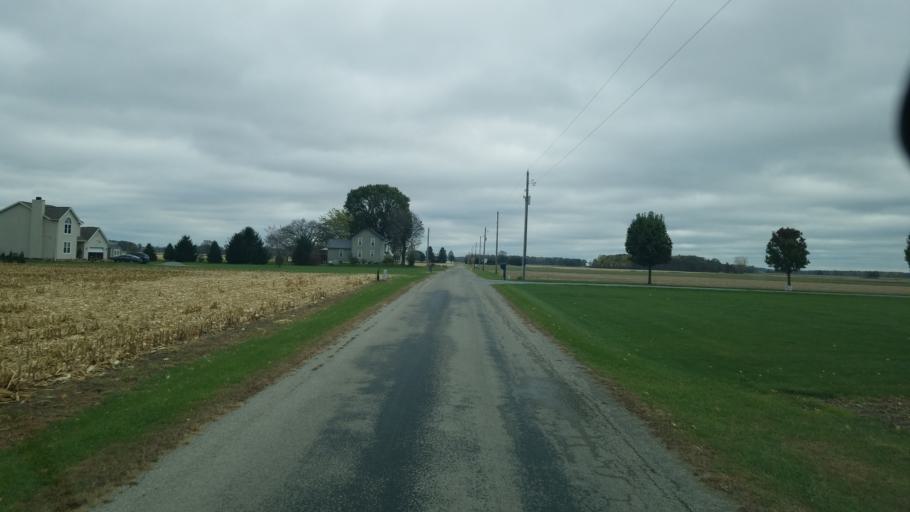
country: US
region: Ohio
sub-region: Huron County
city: Willard
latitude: 40.9314
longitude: -82.8344
